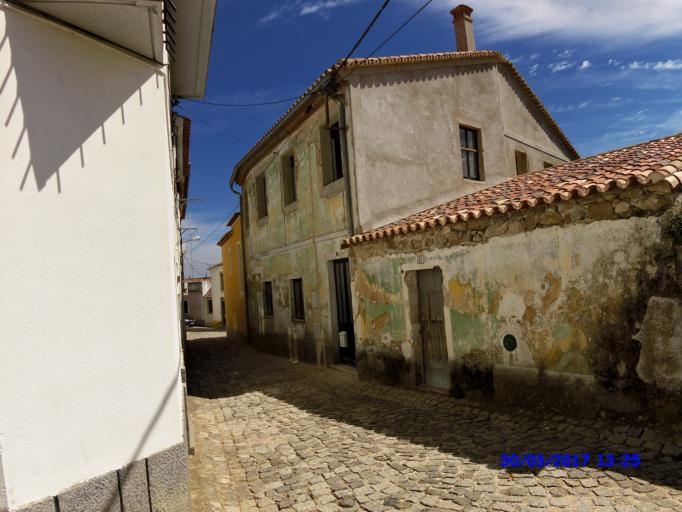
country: PT
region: Faro
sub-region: Monchique
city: Monchique
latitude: 37.3188
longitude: -8.5578
